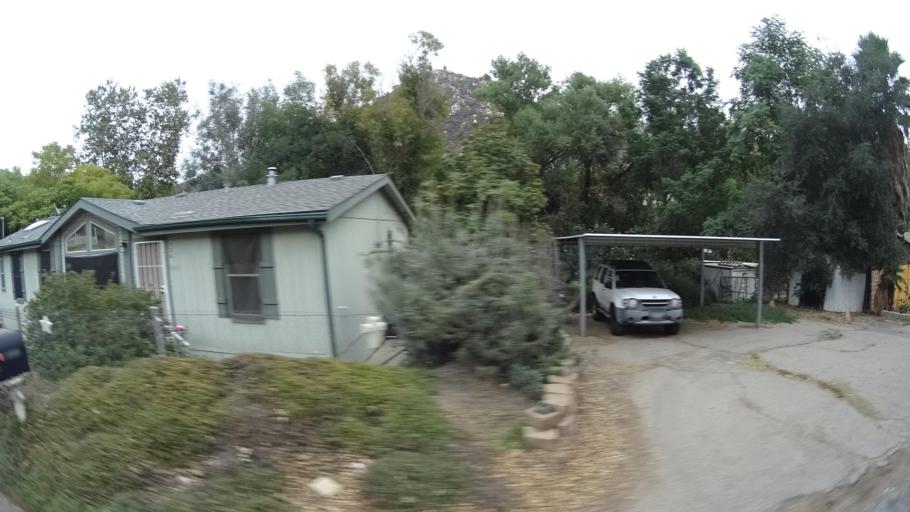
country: US
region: California
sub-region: San Diego County
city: Harbison Canyon
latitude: 32.8166
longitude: -116.8340
